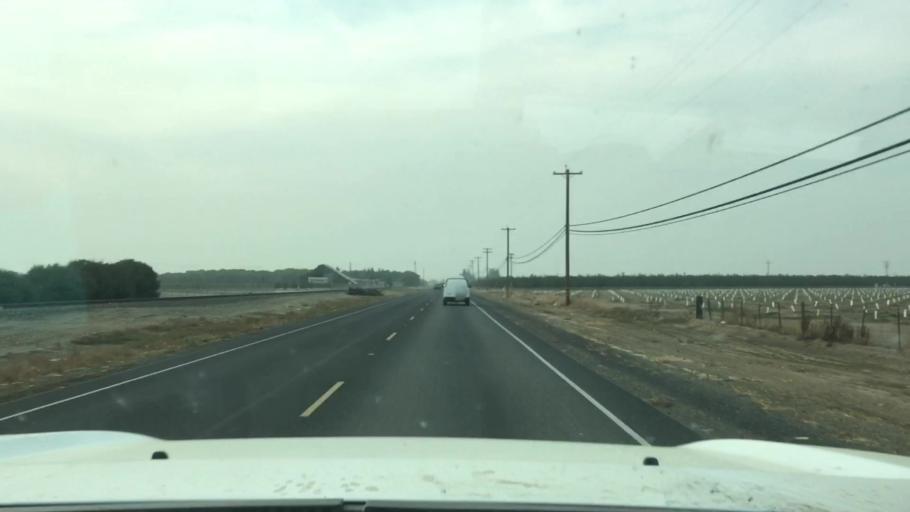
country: US
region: California
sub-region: San Joaquin County
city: Manteca
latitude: 37.8407
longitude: -121.1701
